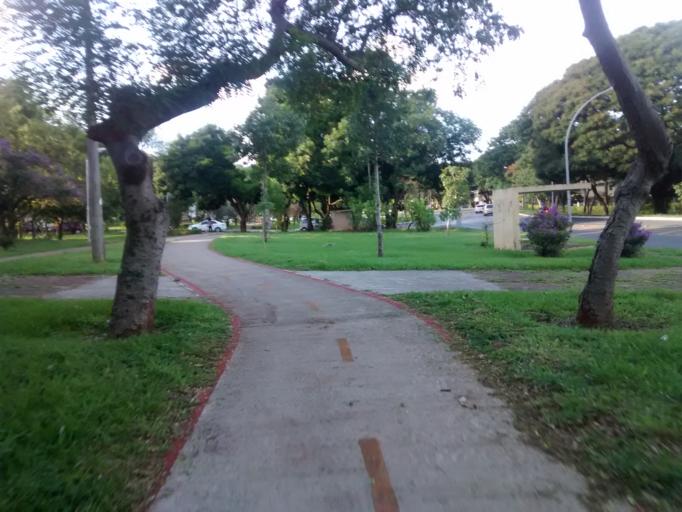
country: BR
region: Federal District
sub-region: Brasilia
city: Brasilia
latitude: -15.7784
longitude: -47.8774
